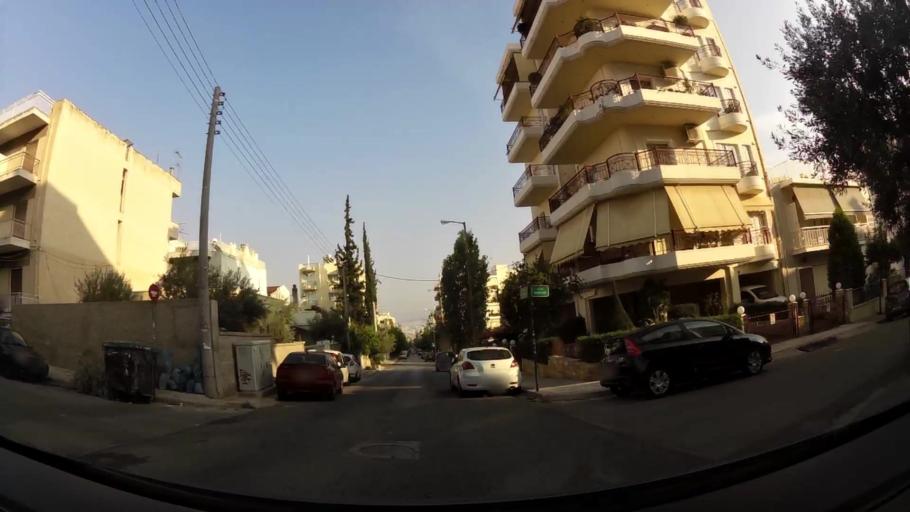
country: GR
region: Attica
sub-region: Nomarchia Athinas
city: Petroupolis
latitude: 38.0430
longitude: 23.6764
